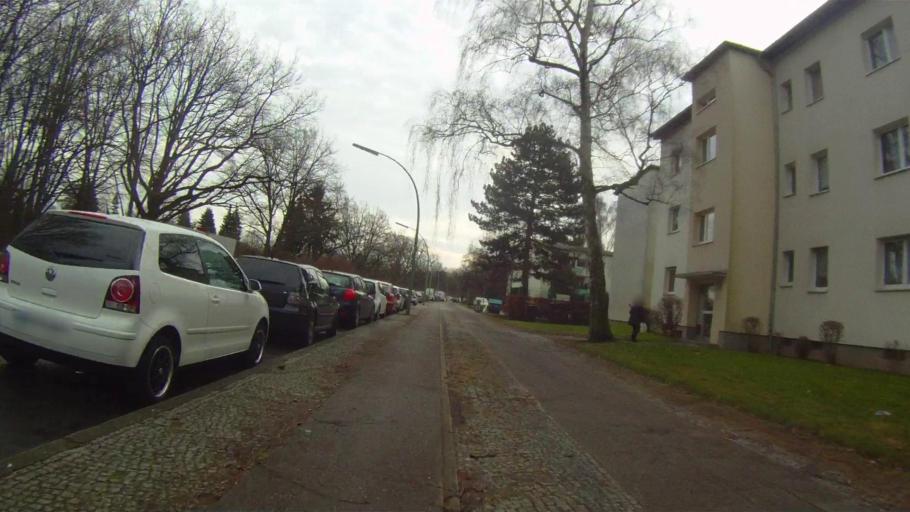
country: DE
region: Berlin
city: Lichtenrade
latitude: 52.4259
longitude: 13.4104
